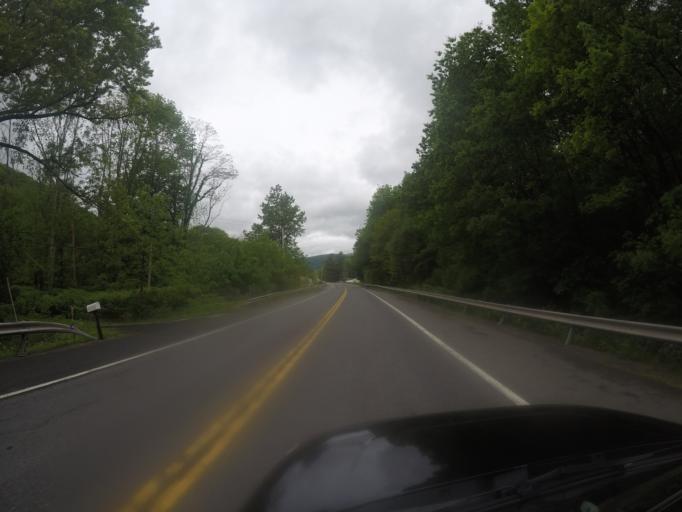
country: US
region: New York
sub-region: Ulster County
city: Shokan
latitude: 42.1140
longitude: -74.3614
